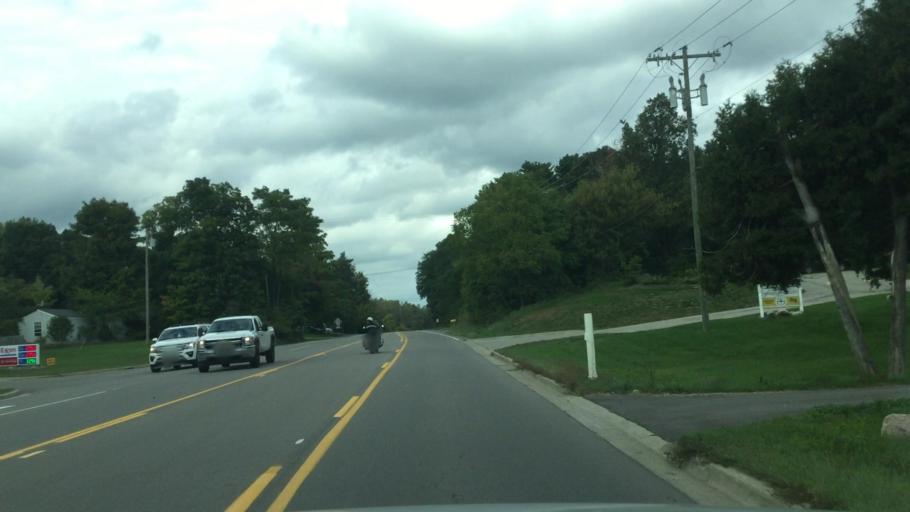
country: US
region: Michigan
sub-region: Livingston County
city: Brighton
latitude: 42.5528
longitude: -83.7530
